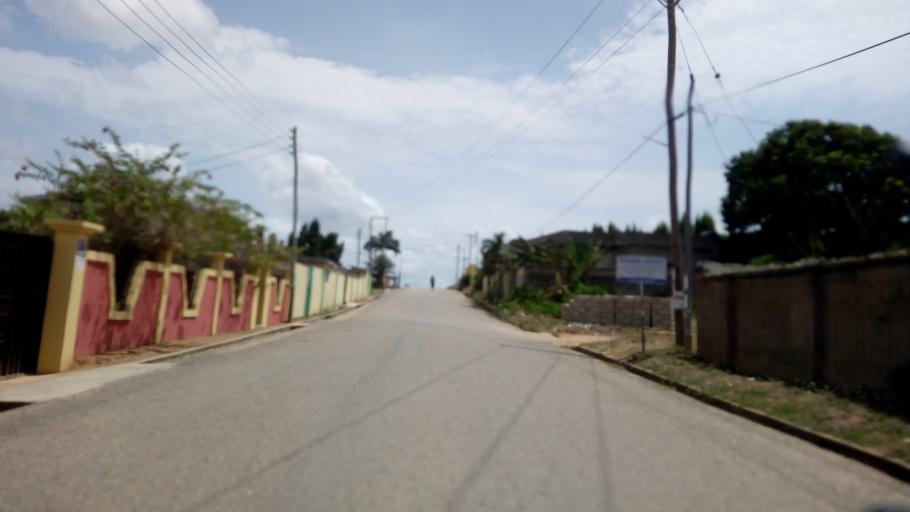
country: GH
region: Central
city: Cape Coast
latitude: 5.1250
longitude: -1.2746
